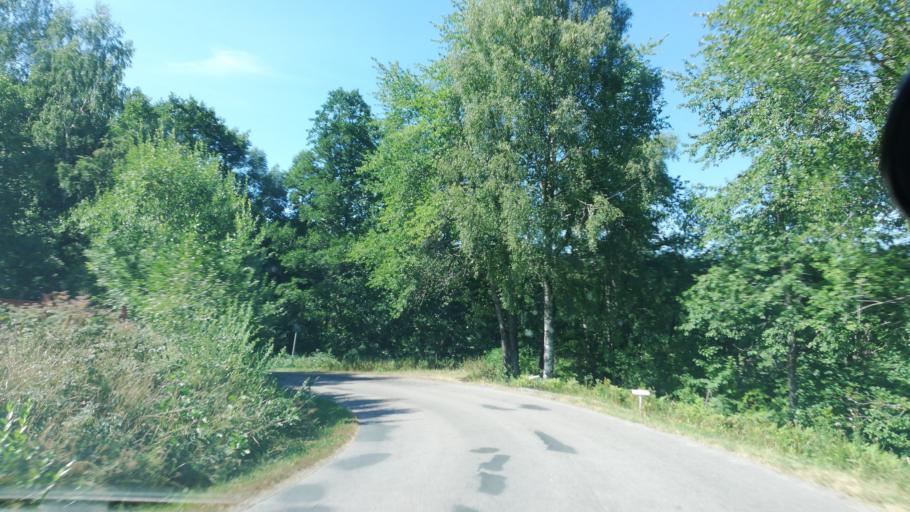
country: SE
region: OEstergoetland
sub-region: Finspangs Kommun
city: Finspang
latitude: 58.7340
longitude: 15.7228
